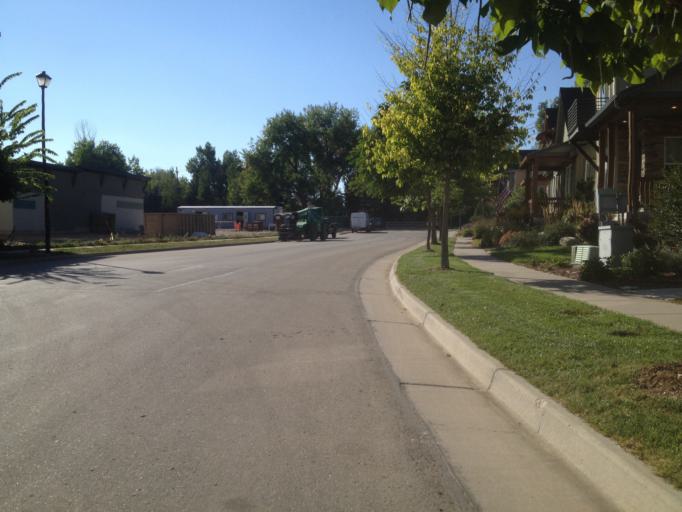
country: US
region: Colorado
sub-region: Boulder County
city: Louisville
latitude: 39.9917
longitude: -105.1257
